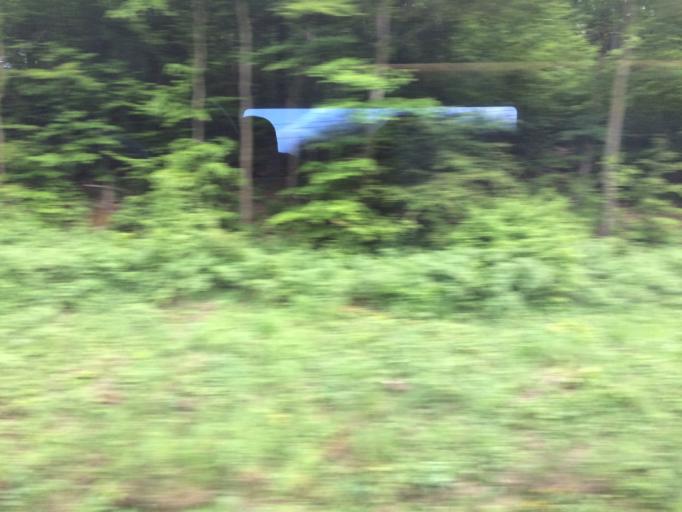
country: DE
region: Bavaria
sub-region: Regierungsbezirk Unterfranken
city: Sailauf
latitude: 50.0051
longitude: 9.2655
